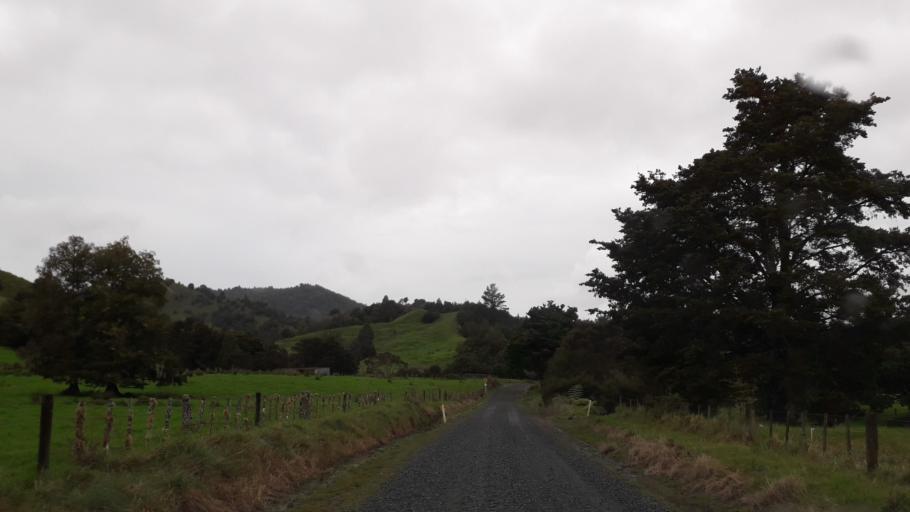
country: NZ
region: Northland
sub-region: Far North District
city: Waimate North
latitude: -35.1515
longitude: 173.7128
